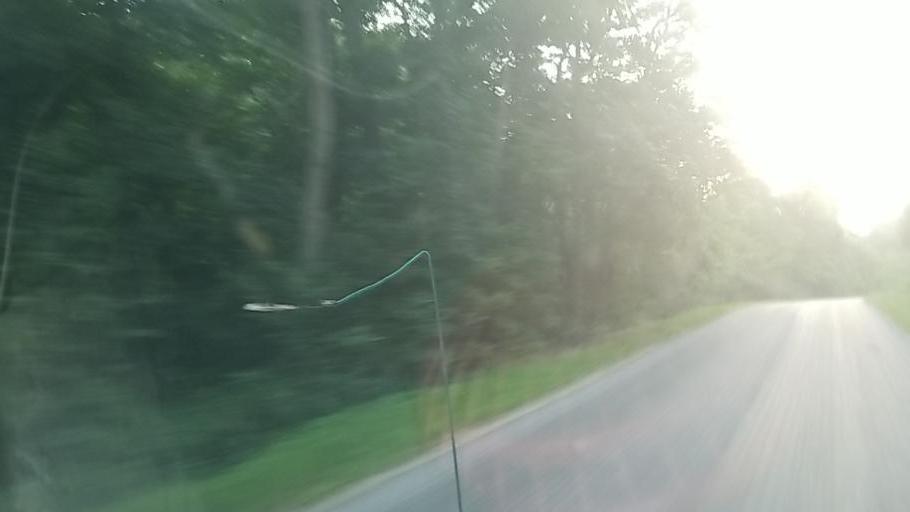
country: US
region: New York
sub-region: Montgomery County
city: Fonda
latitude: 42.9230
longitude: -74.4171
